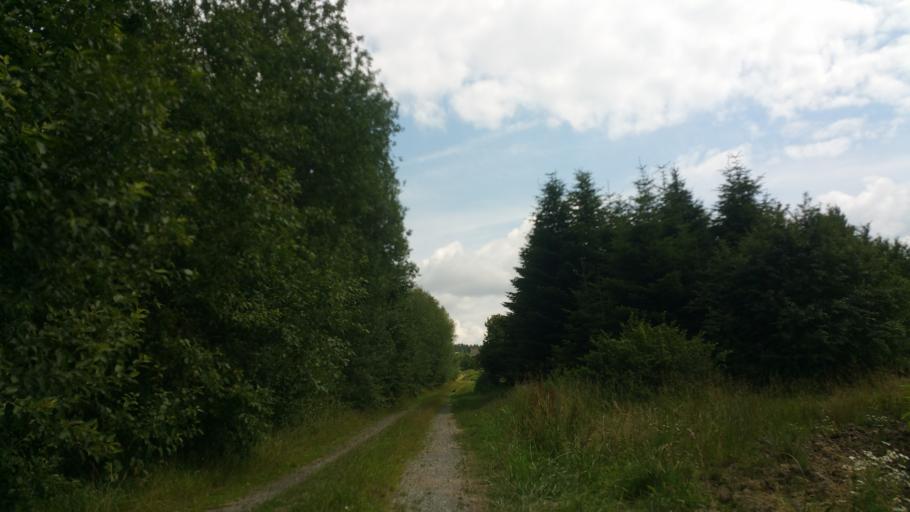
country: DE
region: Bavaria
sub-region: Upper Franconia
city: Schwarzenbach an der Saale
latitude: 50.2045
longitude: 11.9246
